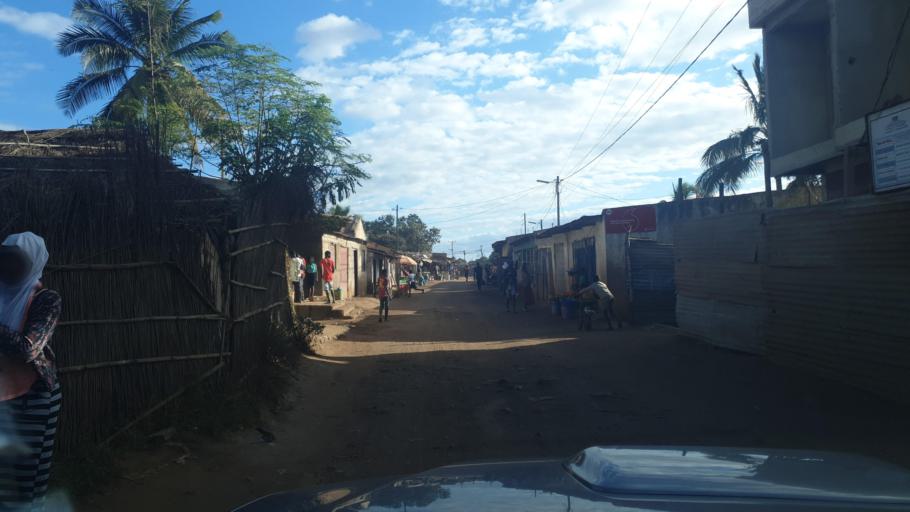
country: MZ
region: Nampula
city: Nampula
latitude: -15.1360
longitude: 39.2697
